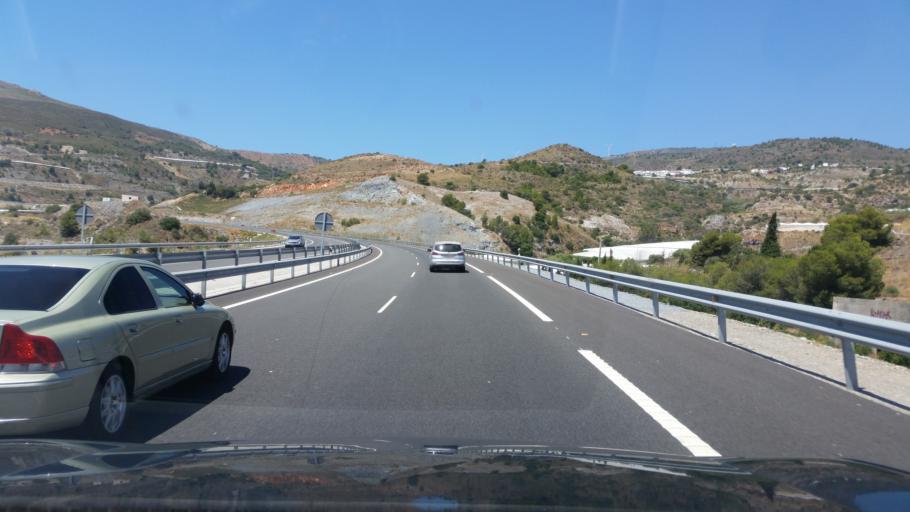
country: ES
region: Andalusia
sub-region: Provincia de Granada
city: Gualchos
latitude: 36.7458
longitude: -3.3723
